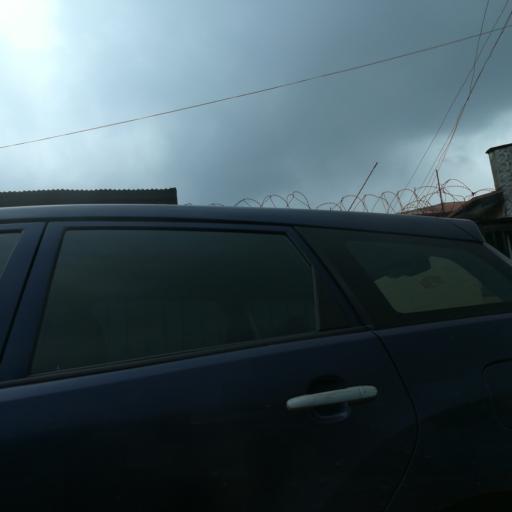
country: NG
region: Lagos
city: Agege
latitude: 6.5969
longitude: 3.2957
